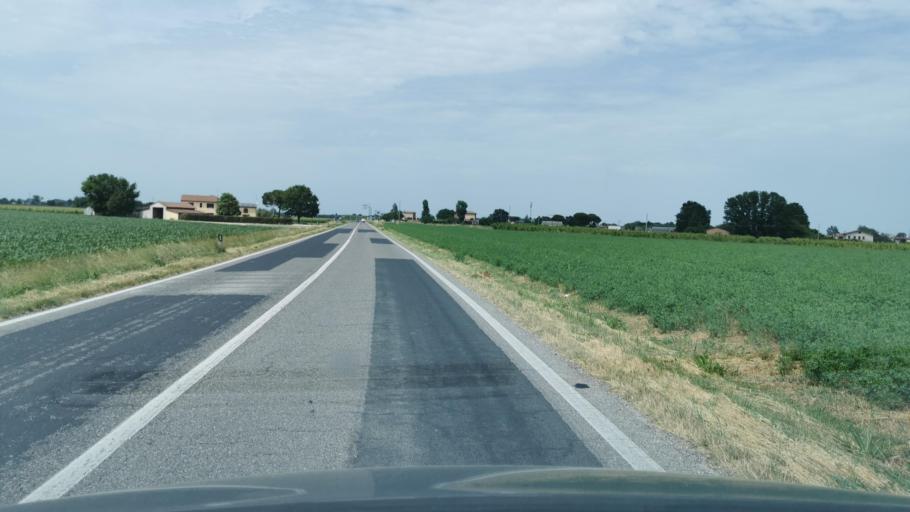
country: IT
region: Emilia-Romagna
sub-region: Provincia di Ravenna
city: Savarna-Conventella
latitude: 44.5050
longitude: 12.1008
